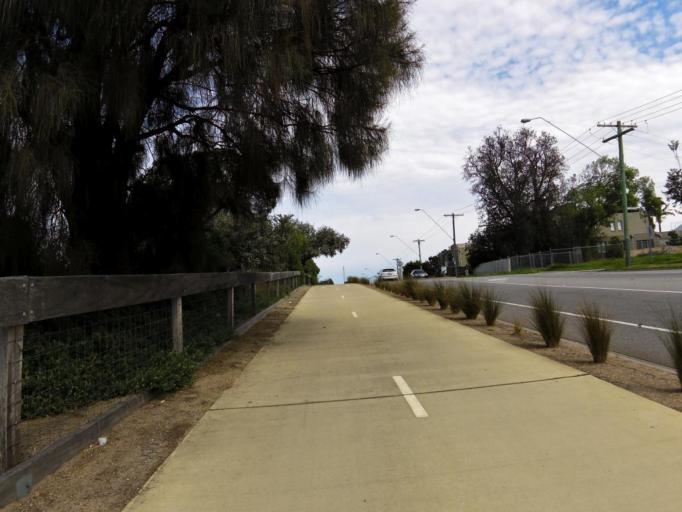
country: AU
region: Victoria
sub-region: Kingston
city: Mentone
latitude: -37.9862
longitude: 145.0514
